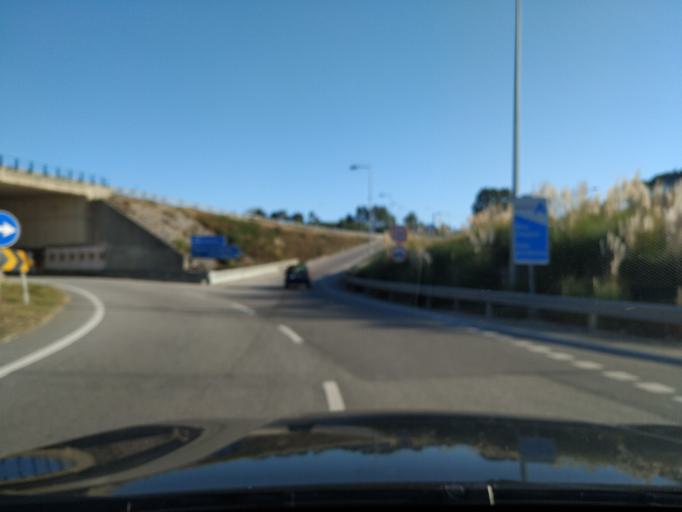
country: PT
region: Porto
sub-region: Vila Nova de Gaia
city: Canelas
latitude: 41.0881
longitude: -8.6032
